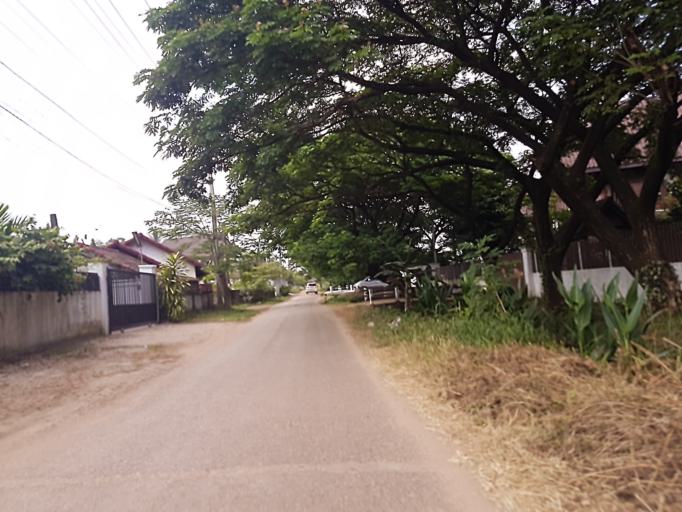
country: LA
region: Vientiane
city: Vientiane
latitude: 17.9248
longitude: 102.6271
